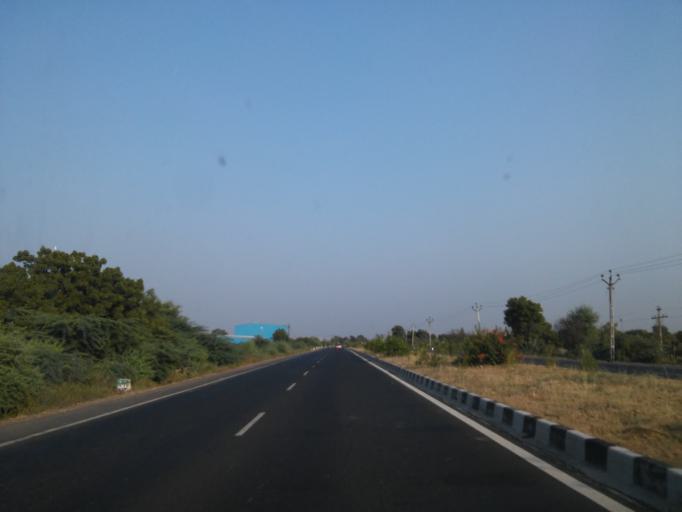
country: IN
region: Gujarat
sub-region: Ahmadabad
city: Sanand
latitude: 23.0829
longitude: 72.1490
